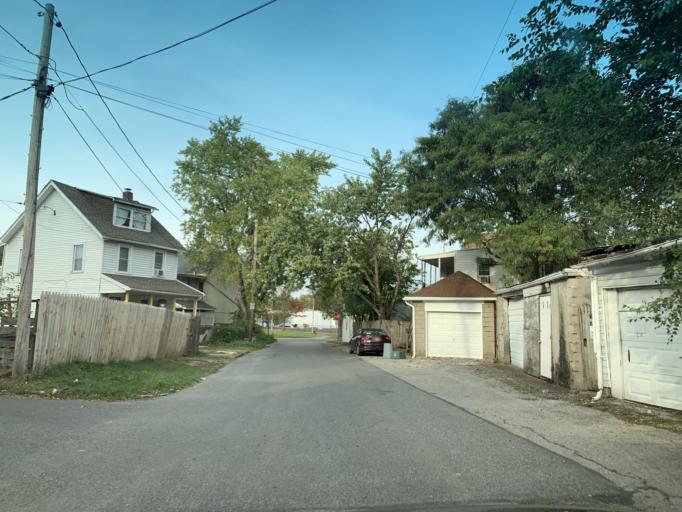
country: US
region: Pennsylvania
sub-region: York County
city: York
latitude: 39.9654
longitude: -76.7356
